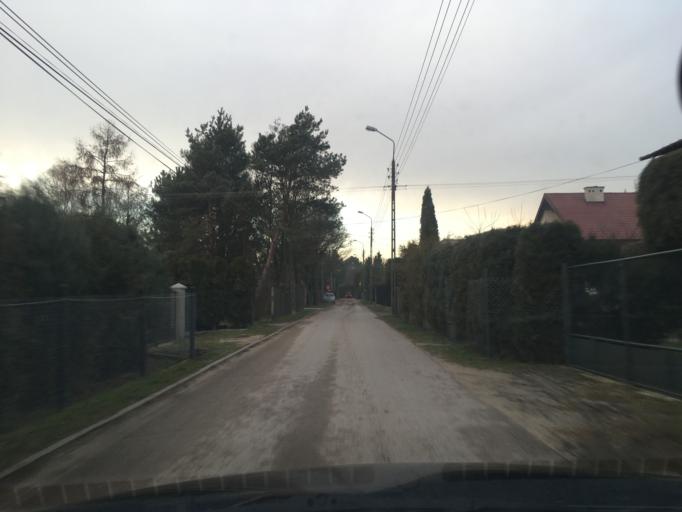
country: PL
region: Masovian Voivodeship
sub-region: Powiat piaseczynski
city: Lesznowola
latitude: 52.0359
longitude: 20.9562
